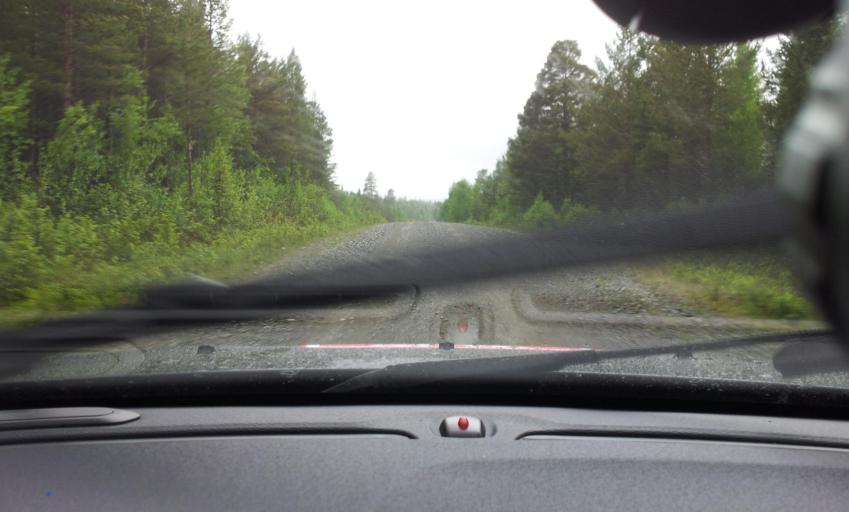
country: SE
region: Jaemtland
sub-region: Are Kommun
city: Are
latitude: 63.1848
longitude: 13.1509
